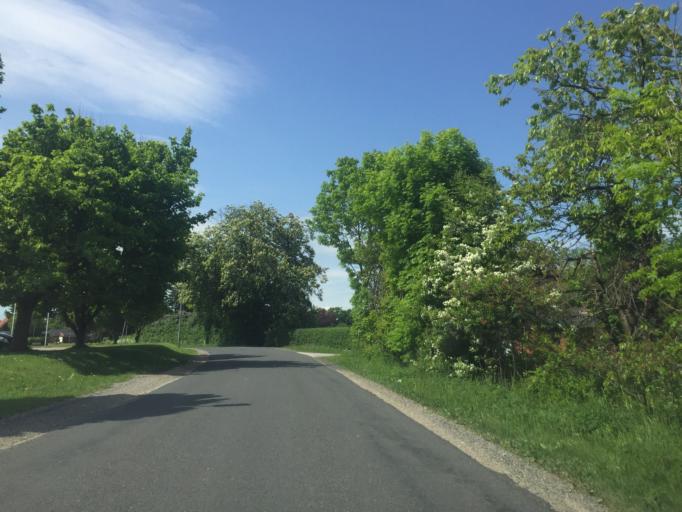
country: DK
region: South Denmark
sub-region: Svendborg Kommune
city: Thuro By
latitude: 55.1486
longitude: 10.7108
